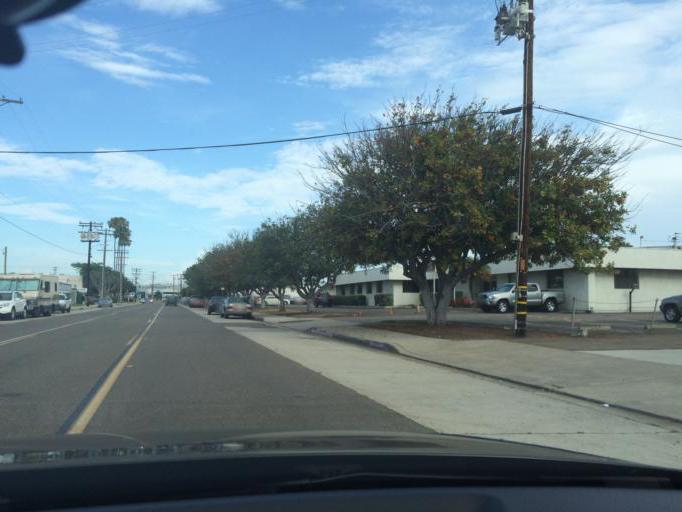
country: US
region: California
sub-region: San Diego County
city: San Diego
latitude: 32.8258
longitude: -117.1519
